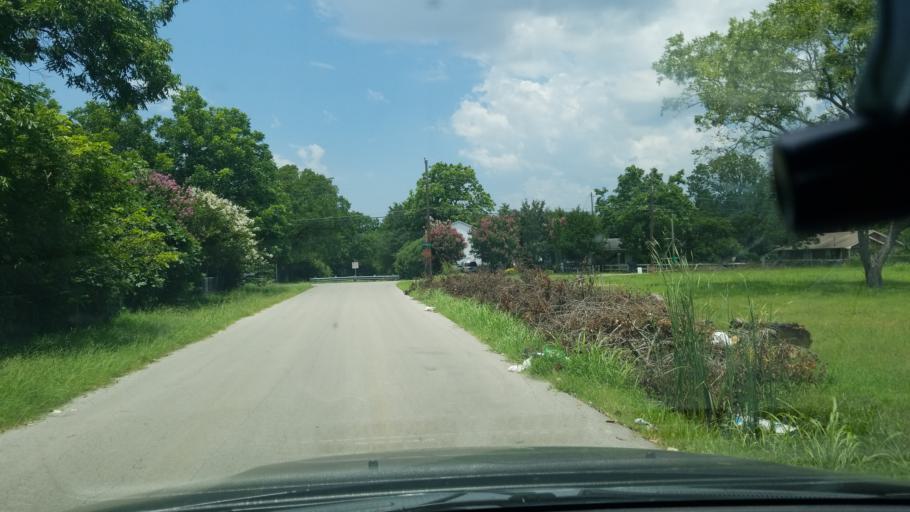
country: US
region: Texas
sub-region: Dallas County
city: Balch Springs
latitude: 32.7164
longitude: -96.6527
